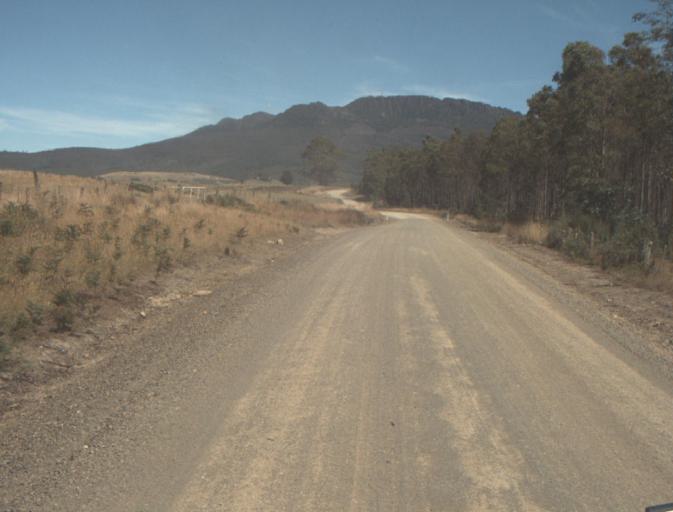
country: AU
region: Tasmania
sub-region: Dorset
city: Scottsdale
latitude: -41.3237
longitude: 147.4456
